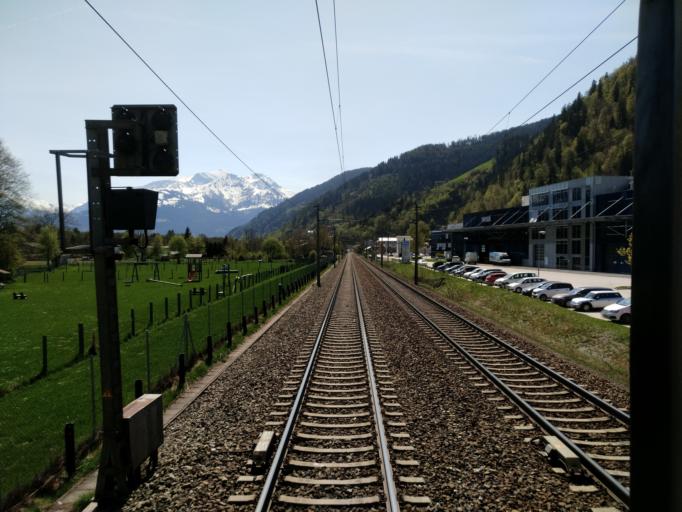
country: AT
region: Salzburg
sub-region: Politischer Bezirk Zell am See
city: Maishofen
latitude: 47.3458
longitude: 12.8023
